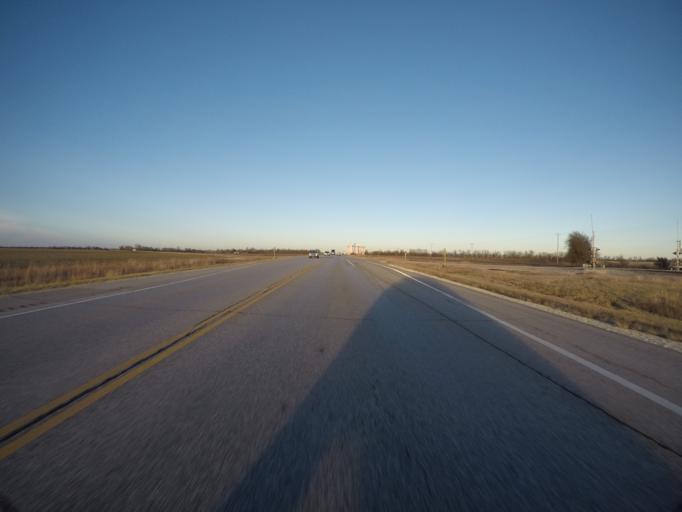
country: US
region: Kansas
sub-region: Harvey County
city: North Newton
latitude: 38.1095
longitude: -97.2656
